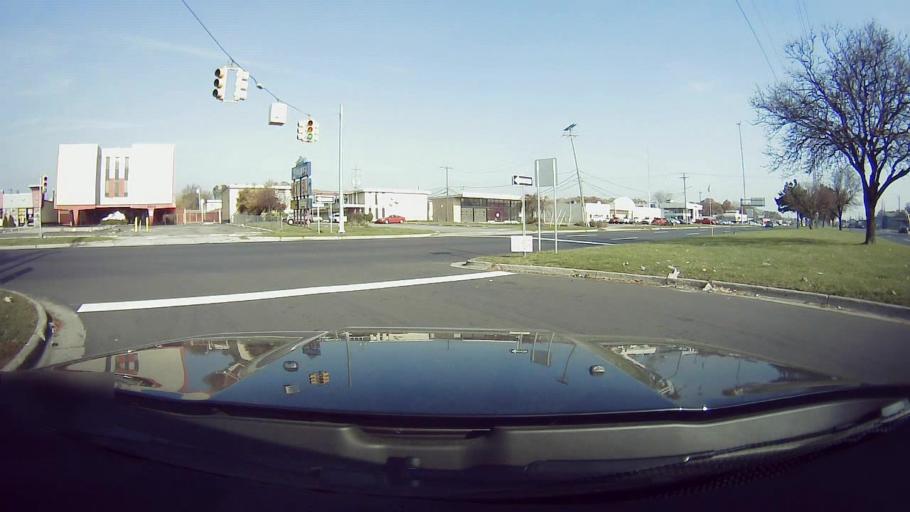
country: US
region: Michigan
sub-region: Oakland County
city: Oak Park
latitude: 42.4449
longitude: -83.1905
